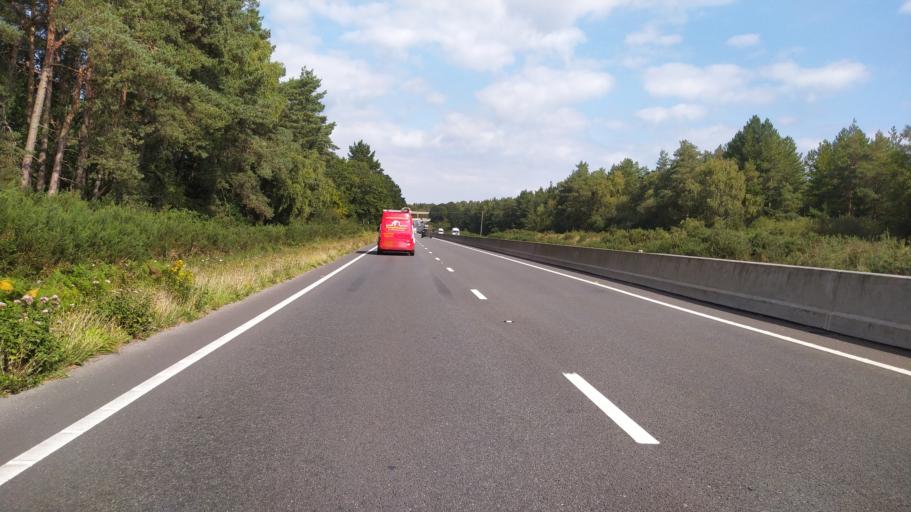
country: GB
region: England
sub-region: Hampshire
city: Ringwood
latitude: 50.8112
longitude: -1.8138
